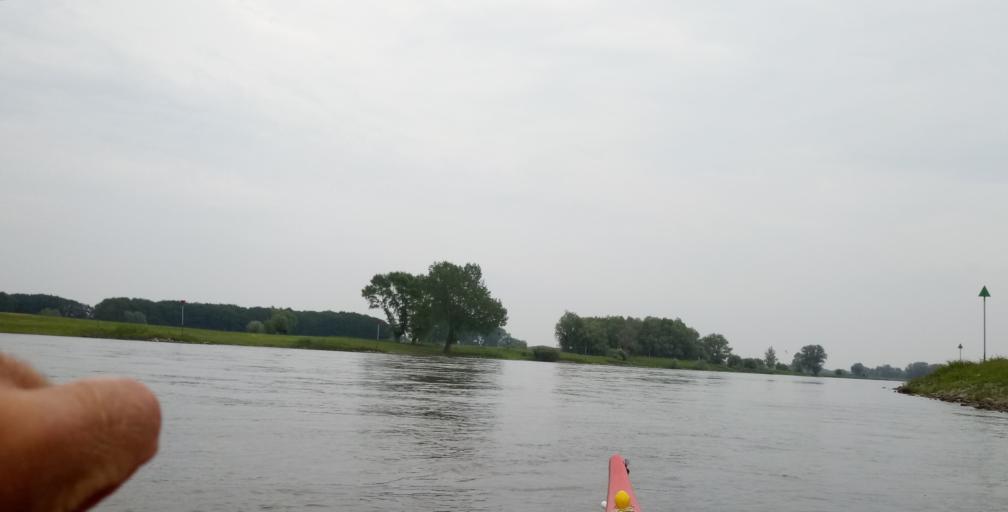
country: NL
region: Gelderland
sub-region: Gemeente Voorst
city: Voorst
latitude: 52.1884
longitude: 6.1699
